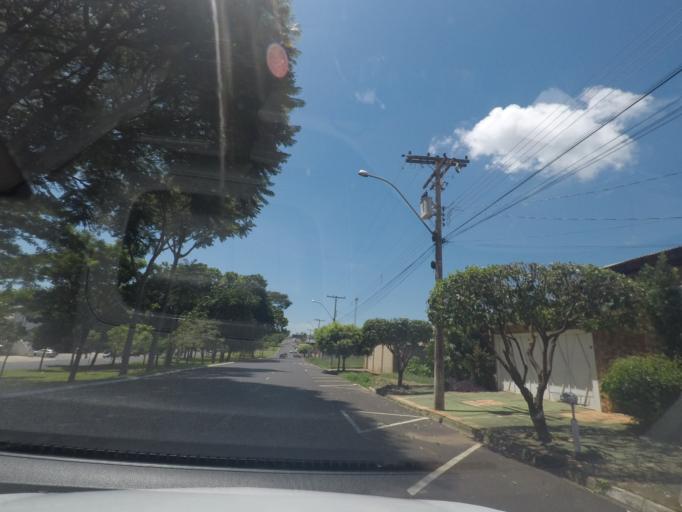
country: BR
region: Sao Paulo
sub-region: Matao
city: Matao
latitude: -21.6179
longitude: -48.3617
